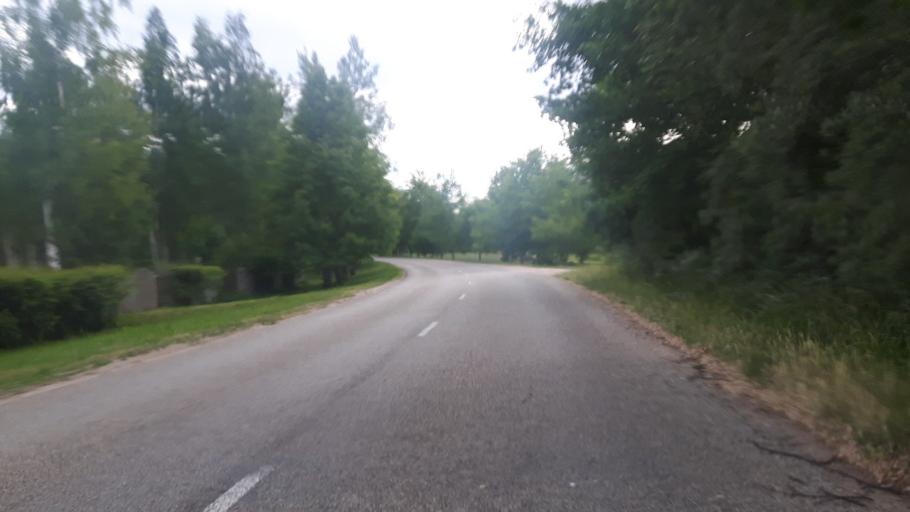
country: LV
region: Engure
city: Smarde
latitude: 57.0337
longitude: 23.3649
